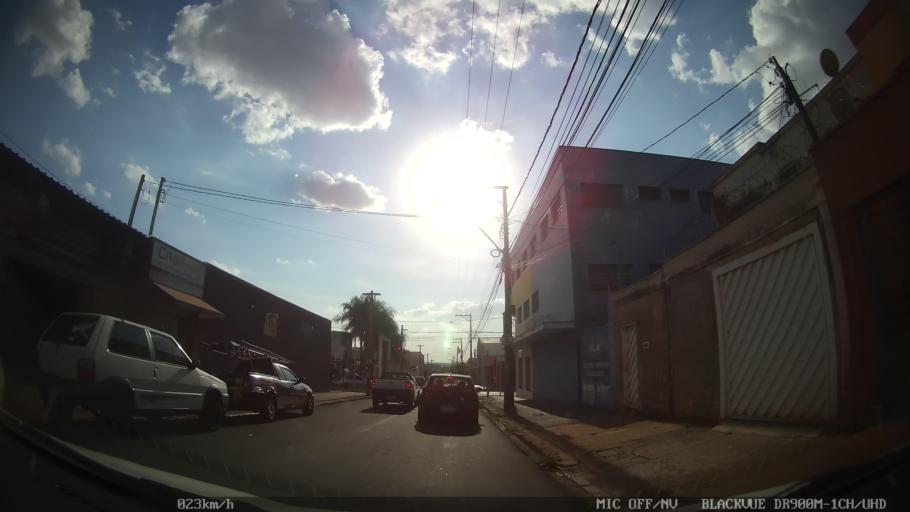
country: BR
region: Sao Paulo
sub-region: Ribeirao Preto
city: Ribeirao Preto
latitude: -21.1670
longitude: -47.8034
